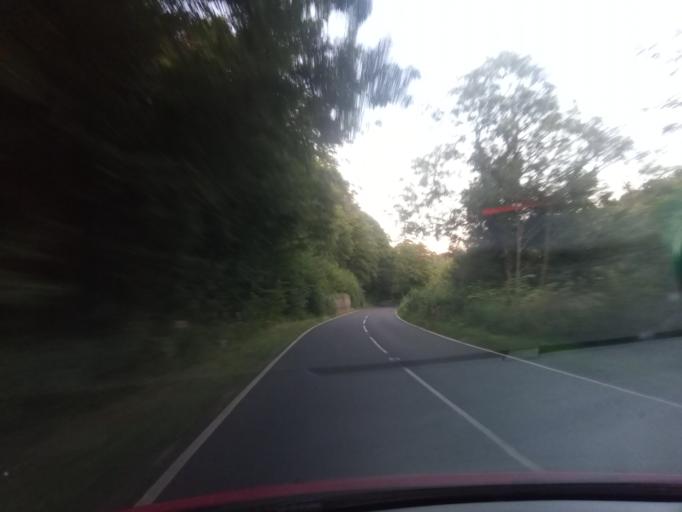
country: GB
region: England
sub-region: Northumberland
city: Bardon Mill
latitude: 54.9185
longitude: -2.3306
